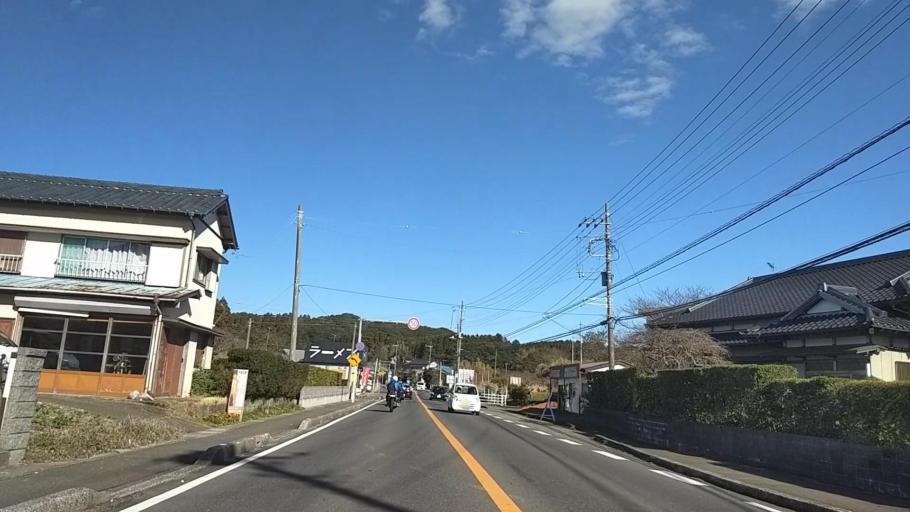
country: JP
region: Chiba
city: Ohara
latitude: 35.2225
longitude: 140.3837
